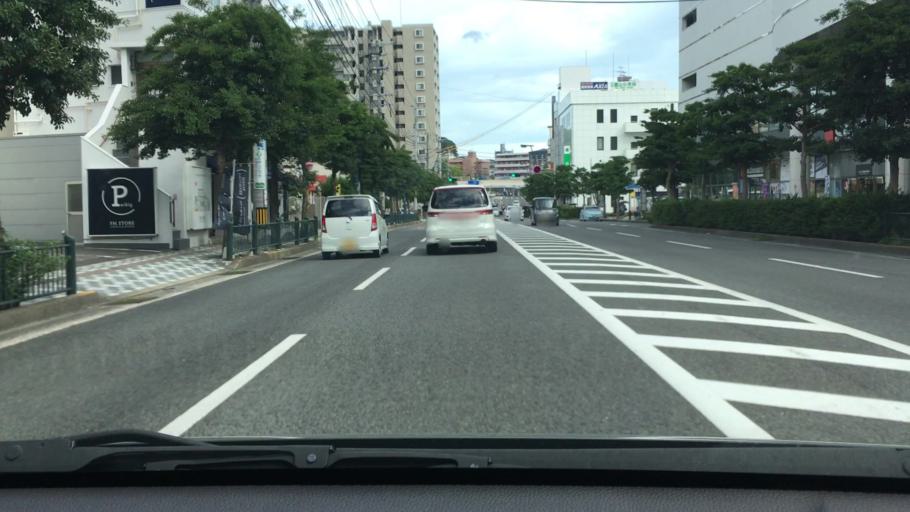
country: JP
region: Nagasaki
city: Togitsu
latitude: 32.8044
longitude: 129.8510
